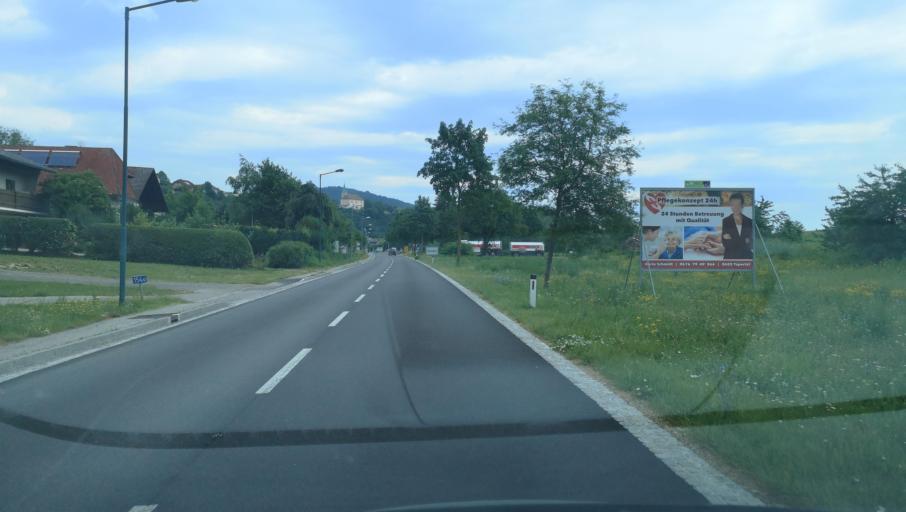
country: AT
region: Lower Austria
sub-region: Politischer Bezirk Melk
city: Leiben
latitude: 48.2242
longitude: 15.2549
